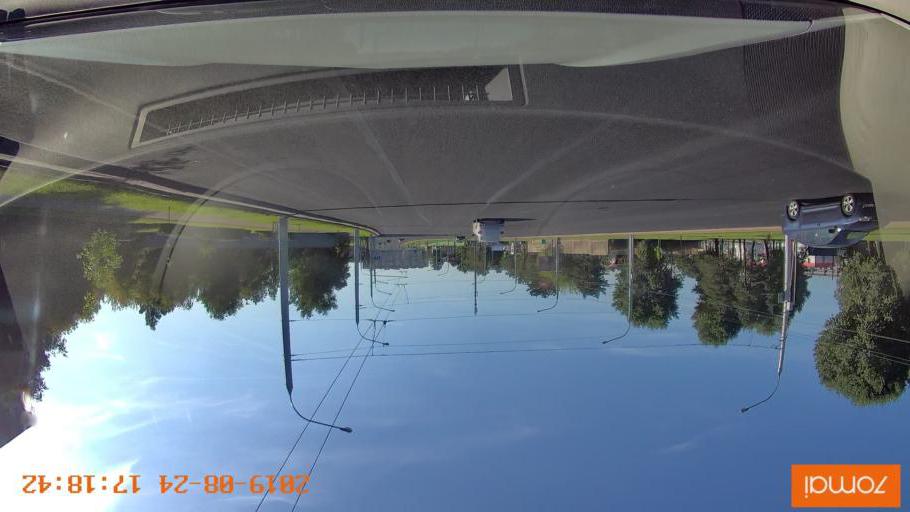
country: BY
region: Minsk
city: Vyaliki Trastsyanets
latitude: 53.8674
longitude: 27.6455
